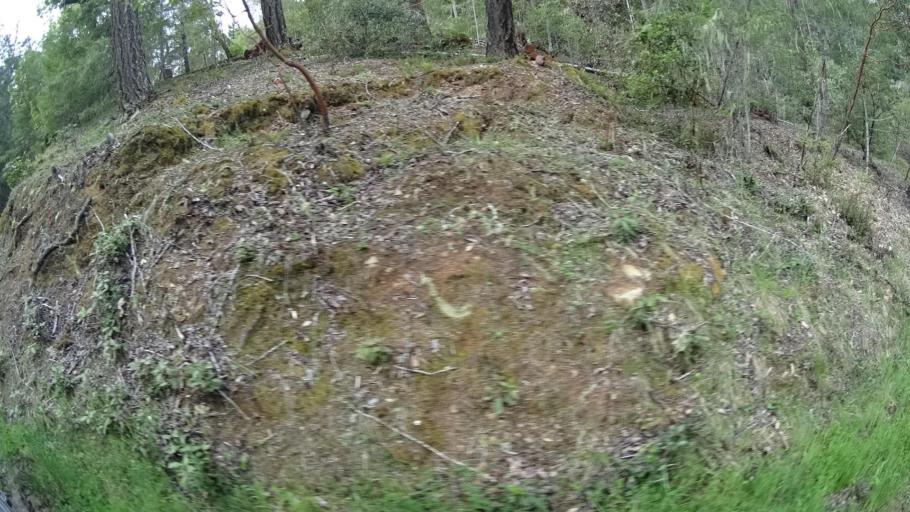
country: US
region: California
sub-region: Humboldt County
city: Redway
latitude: 40.1386
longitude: -123.6295
